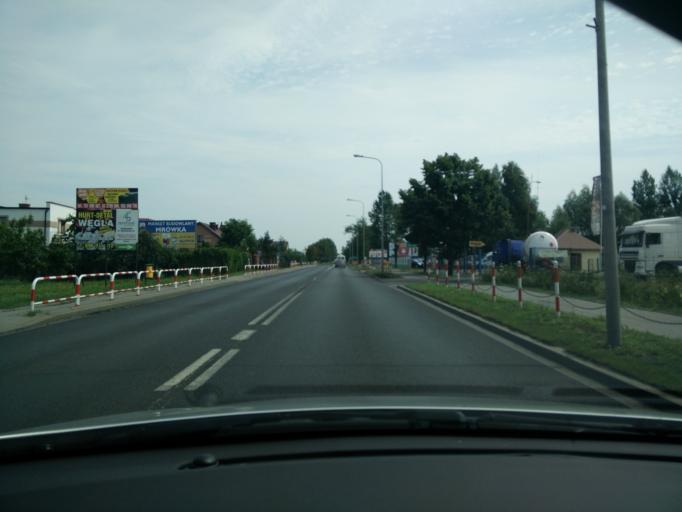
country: PL
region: Greater Poland Voivodeship
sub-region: Powiat slupecki
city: Strzalkowo
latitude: 52.3069
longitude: 17.8267
